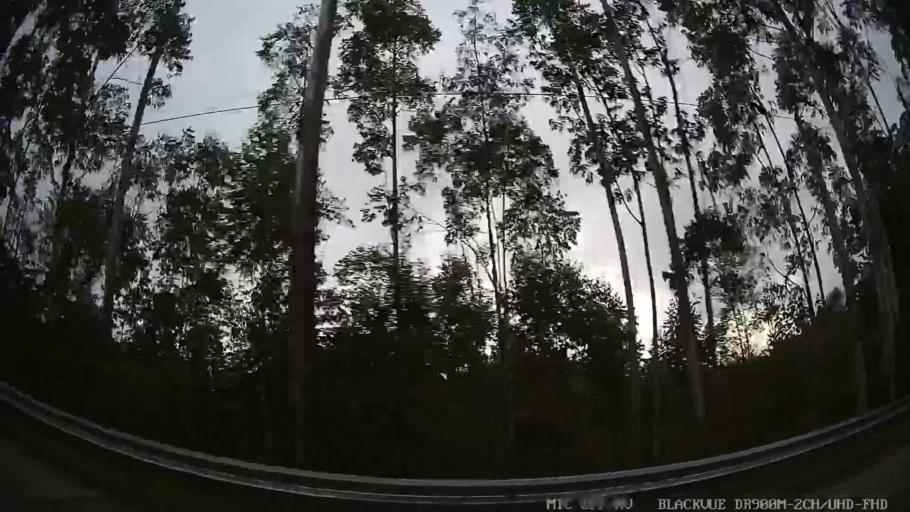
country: BR
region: Sao Paulo
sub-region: Caraguatatuba
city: Caraguatatuba
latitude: -23.5243
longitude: -45.5375
